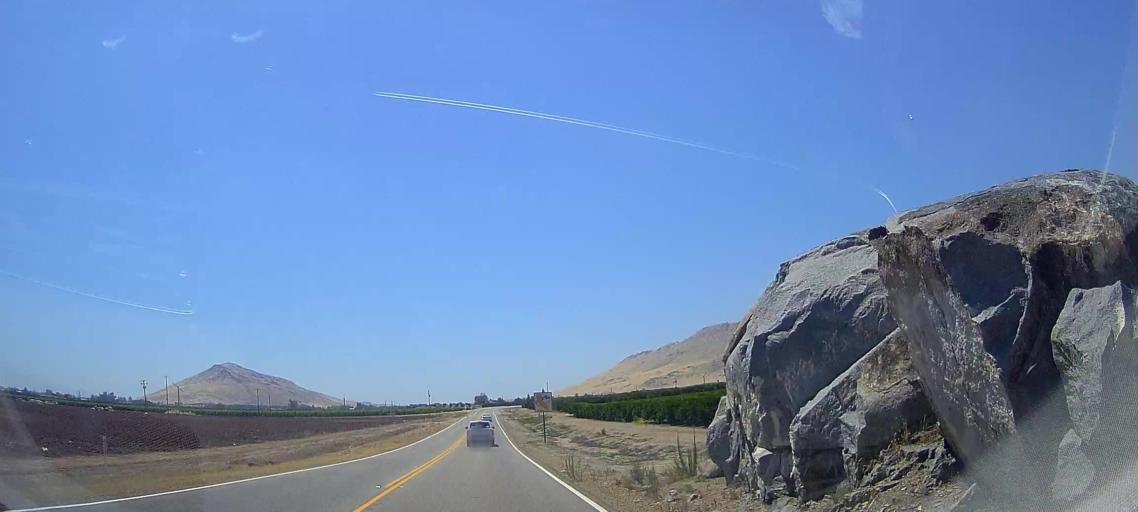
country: US
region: California
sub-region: Fresno County
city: Orange Cove
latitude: 36.7155
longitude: -119.3548
